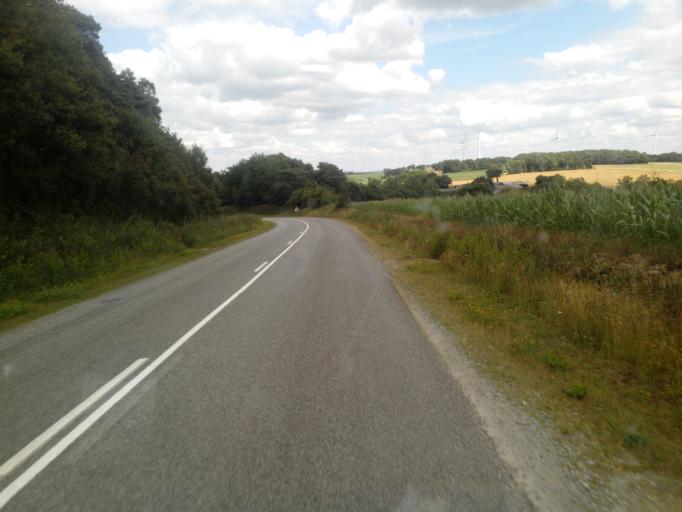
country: FR
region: Brittany
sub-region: Departement du Morbihan
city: Taupont
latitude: 48.0050
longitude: -2.4907
